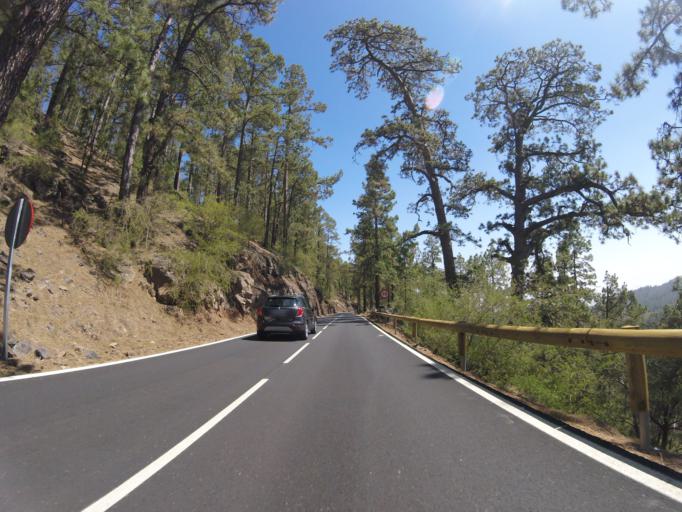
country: ES
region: Canary Islands
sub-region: Provincia de Santa Cruz de Tenerife
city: Vilaflor
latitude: 28.1683
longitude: -16.6355
